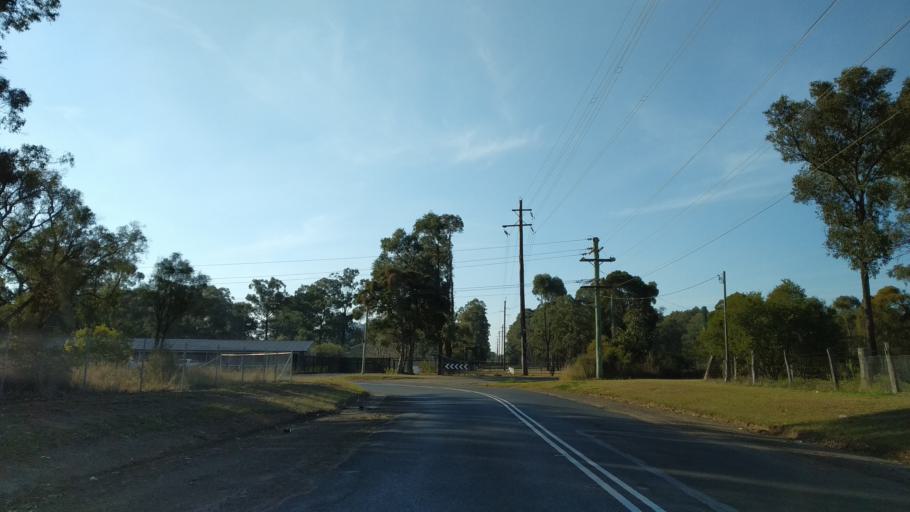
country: AU
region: New South Wales
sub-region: Penrith Municipality
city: Werrington Downs
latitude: -33.6929
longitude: 150.7348
